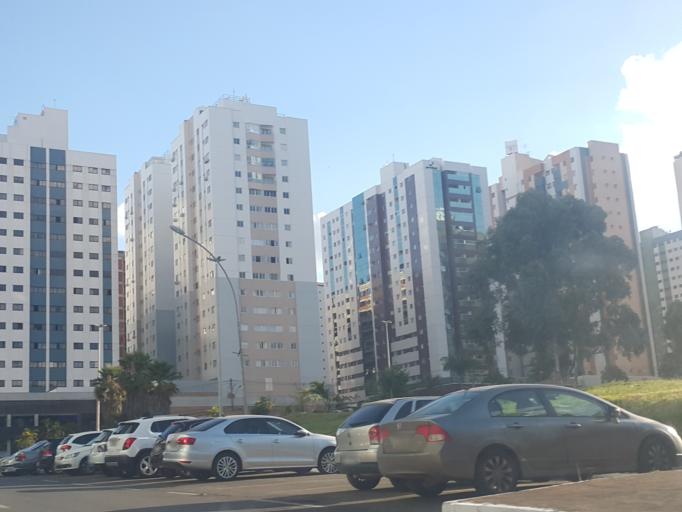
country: BR
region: Federal District
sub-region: Brasilia
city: Brasilia
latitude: -15.8389
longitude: -48.0346
